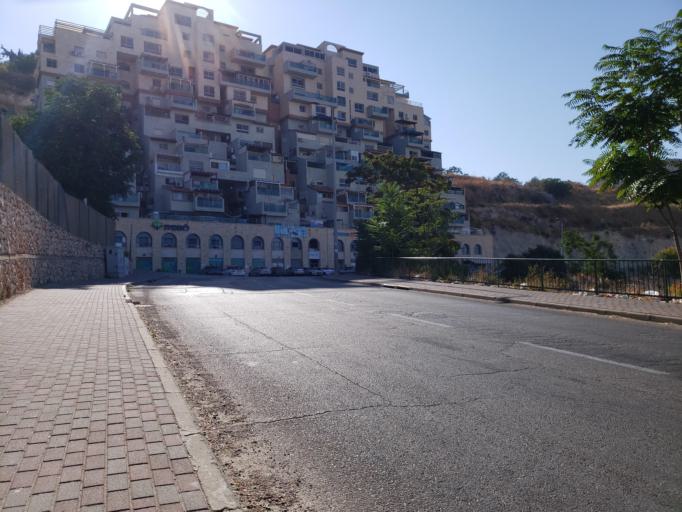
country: IL
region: Northern District
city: Safed
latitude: 32.9650
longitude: 35.4914
